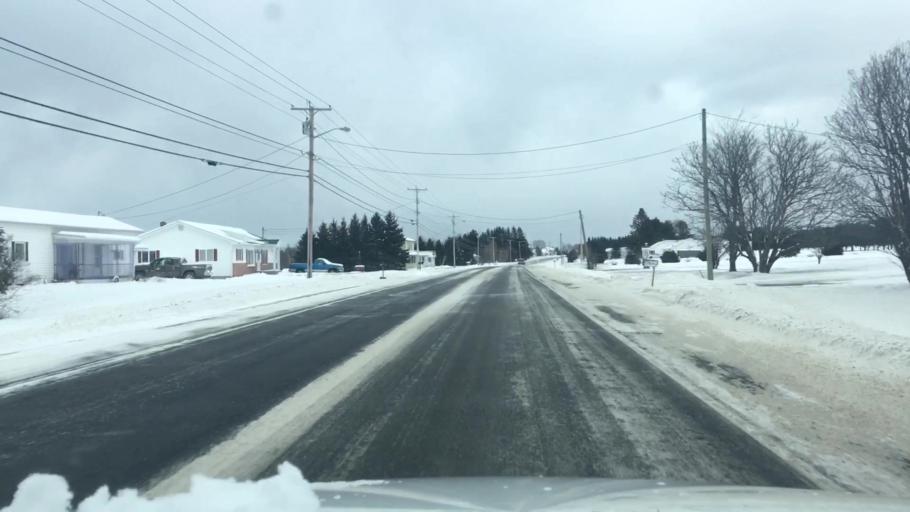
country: US
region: Maine
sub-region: Aroostook County
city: Madawaska
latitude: 47.3452
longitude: -68.2514
